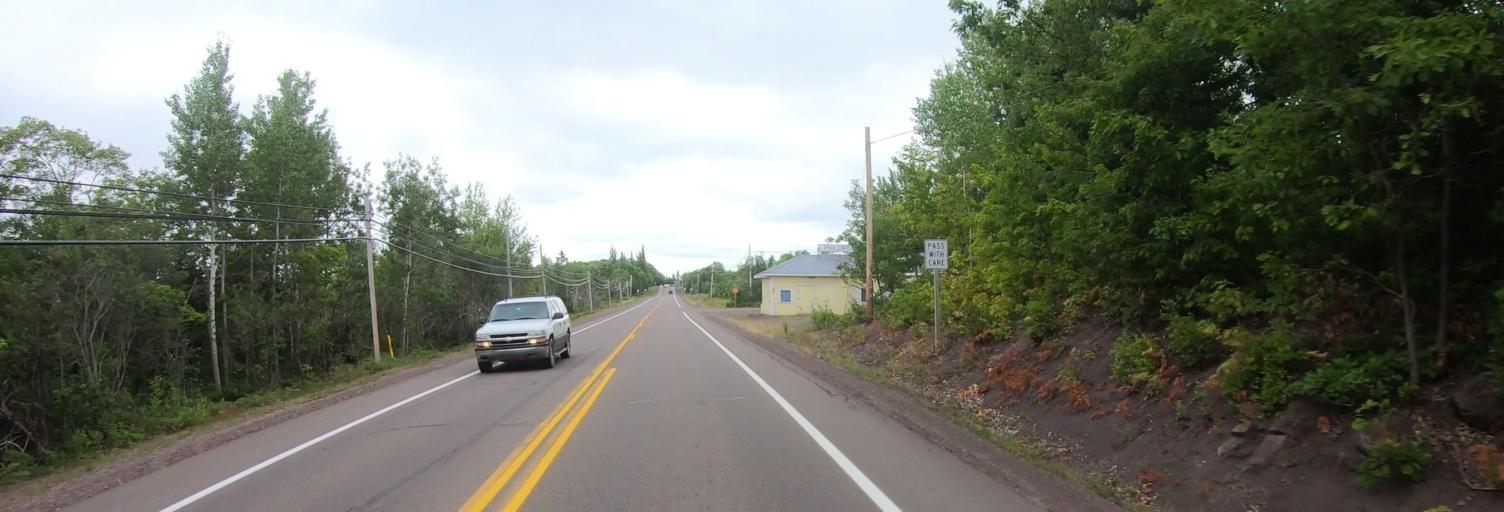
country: US
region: Michigan
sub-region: Houghton County
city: Laurium
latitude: 47.2795
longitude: -88.4128
